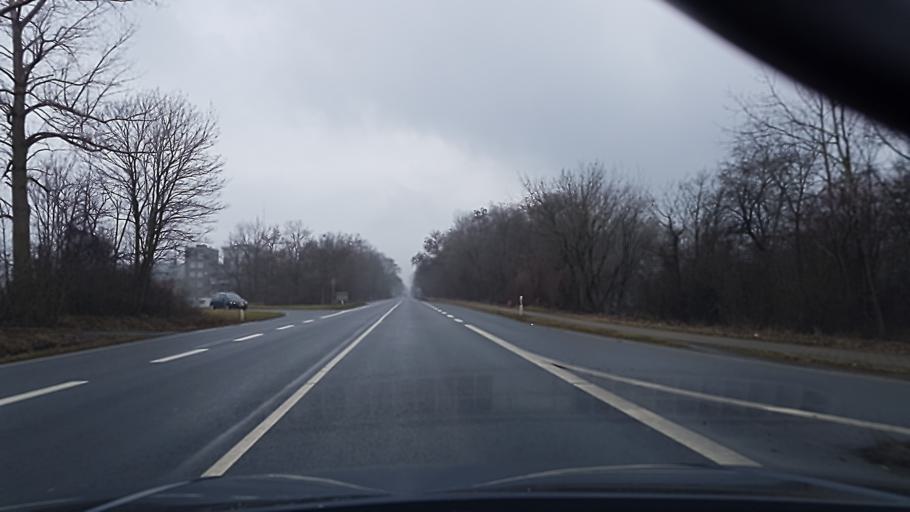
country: DE
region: Lower Saxony
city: Cramme
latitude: 52.1647
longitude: 10.4343
